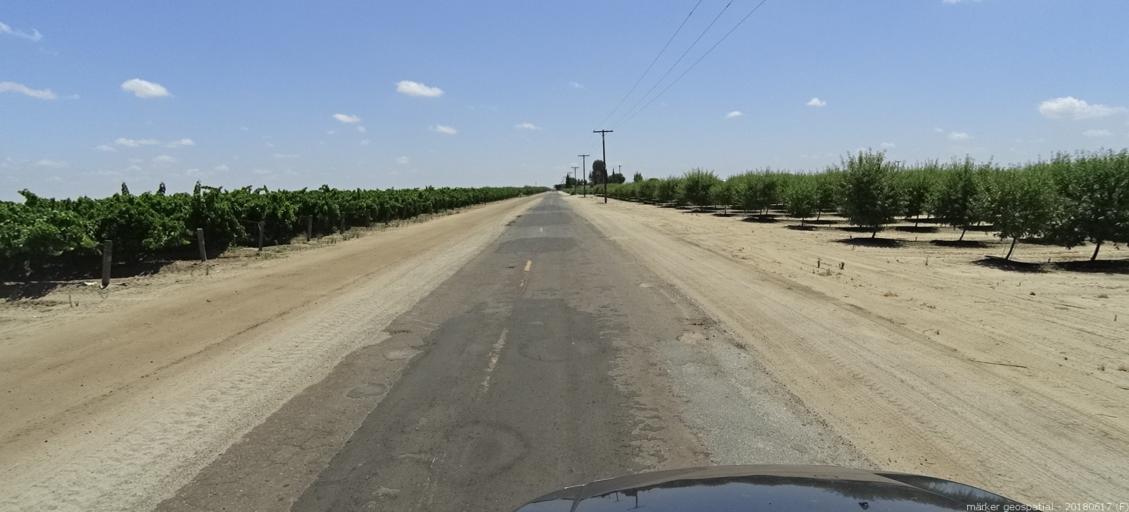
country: US
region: California
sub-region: Fresno County
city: Kerman
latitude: 36.8166
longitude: -120.1509
